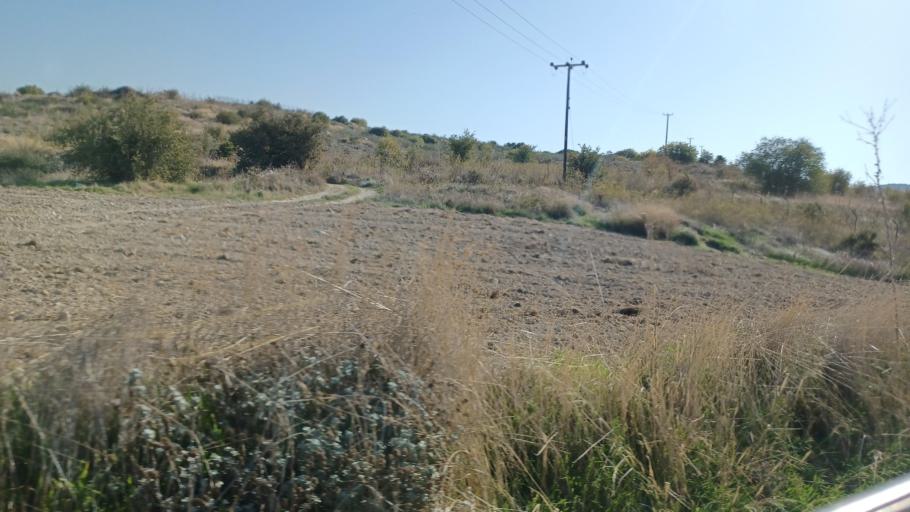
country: CY
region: Pafos
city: Polis
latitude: 35.0397
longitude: 32.4630
